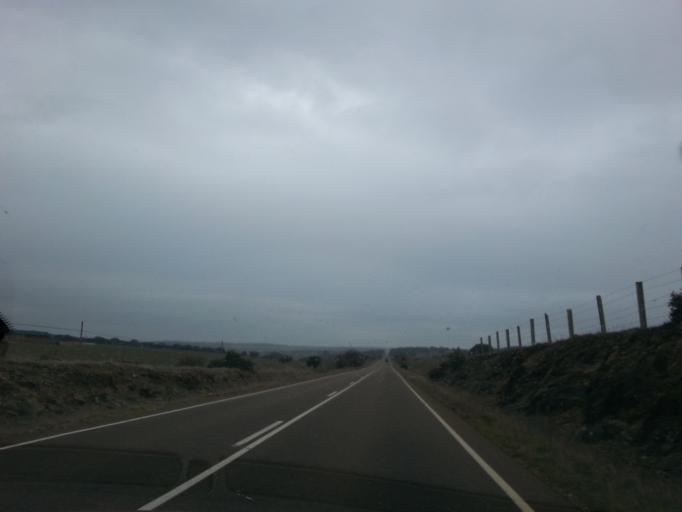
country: ES
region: Castille and Leon
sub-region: Provincia de Salamanca
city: Tamames
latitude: 40.6724
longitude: -6.0767
